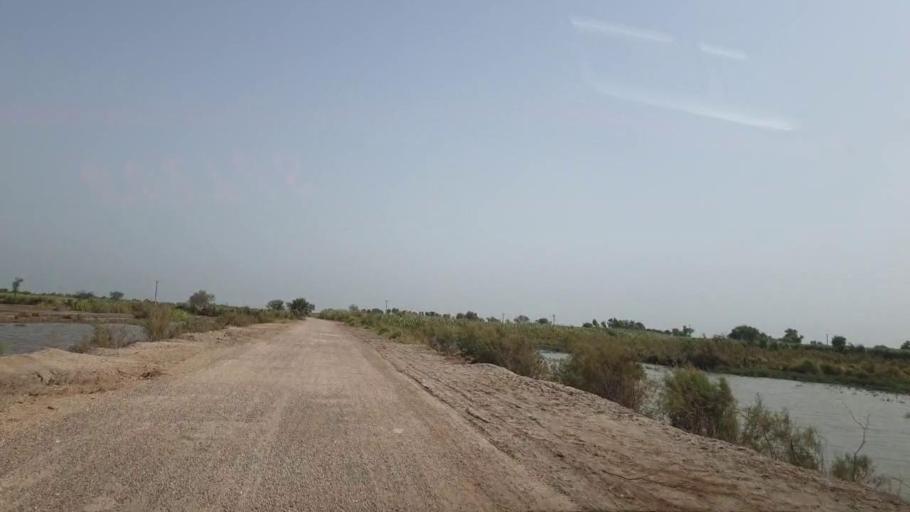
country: PK
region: Sindh
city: Sakrand
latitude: 26.3037
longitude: 68.2202
